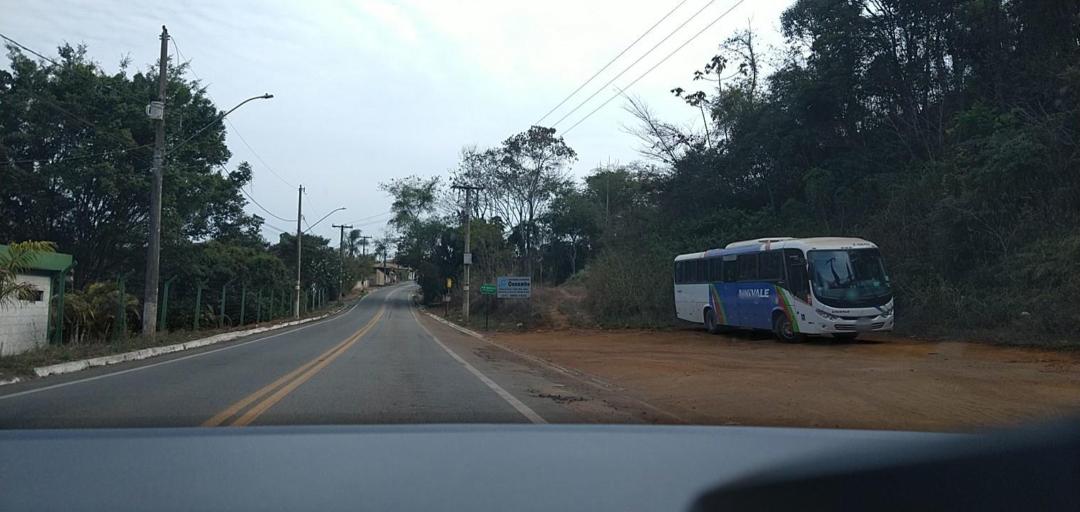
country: BR
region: Minas Gerais
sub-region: Rio Piracicaba
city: Rio Piracicaba
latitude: -19.8946
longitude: -43.1435
